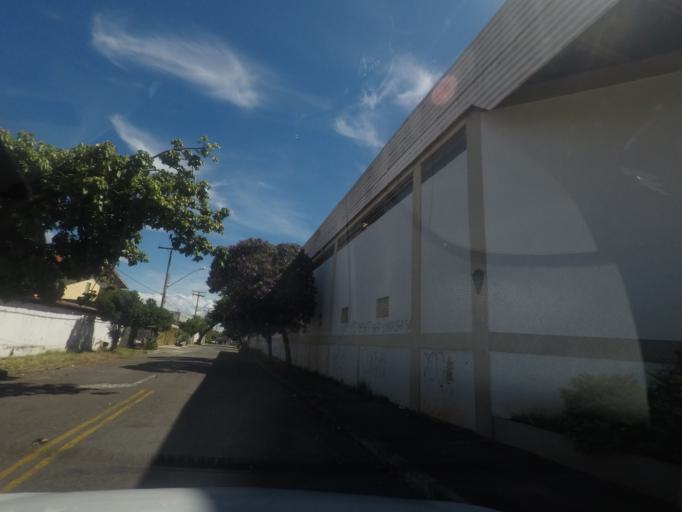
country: BR
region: Goias
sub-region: Goiania
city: Goiania
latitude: -16.6757
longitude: -49.2746
